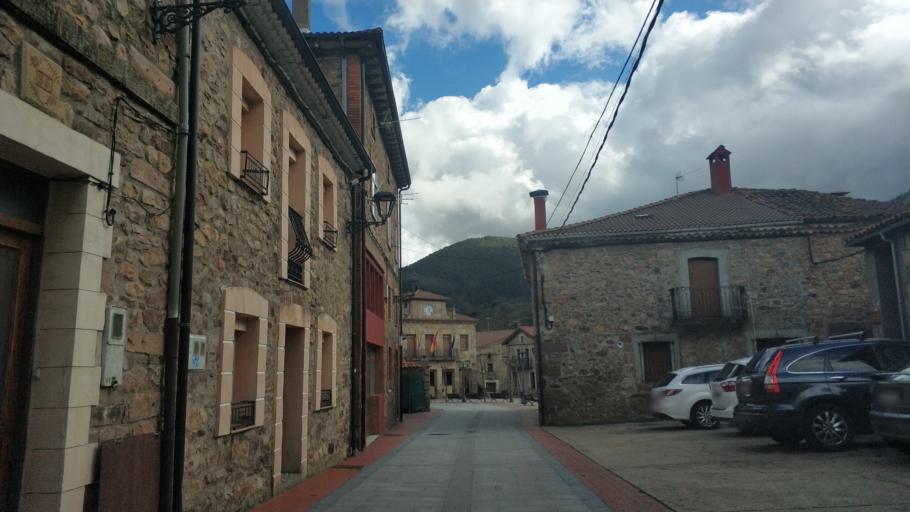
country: ES
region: Castille and Leon
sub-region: Provincia de Burgos
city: Neila
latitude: 42.0604
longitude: -2.9977
